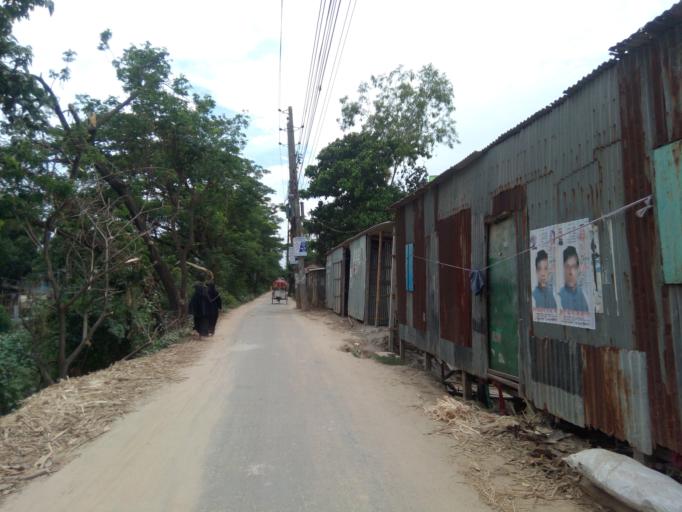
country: BD
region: Dhaka
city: Paltan
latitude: 23.7568
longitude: 90.4575
